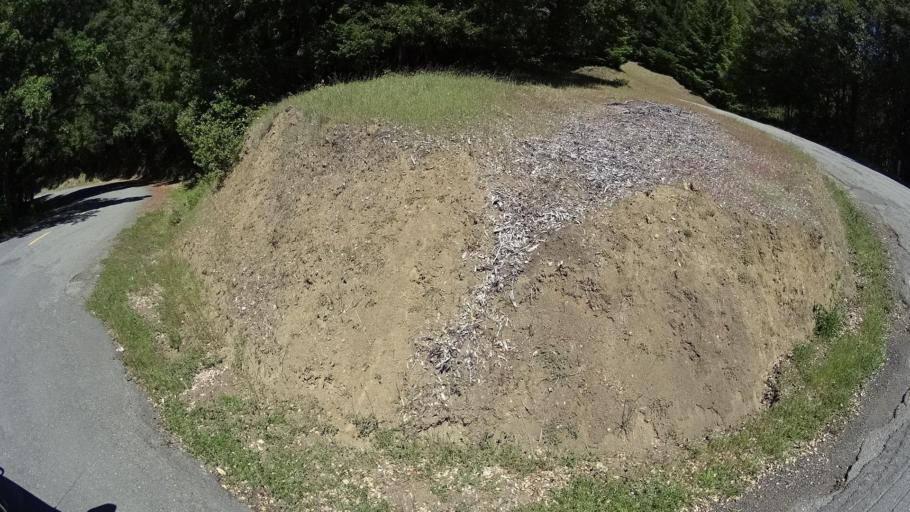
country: US
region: California
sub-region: Humboldt County
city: Rio Dell
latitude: 40.2525
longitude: -124.1180
